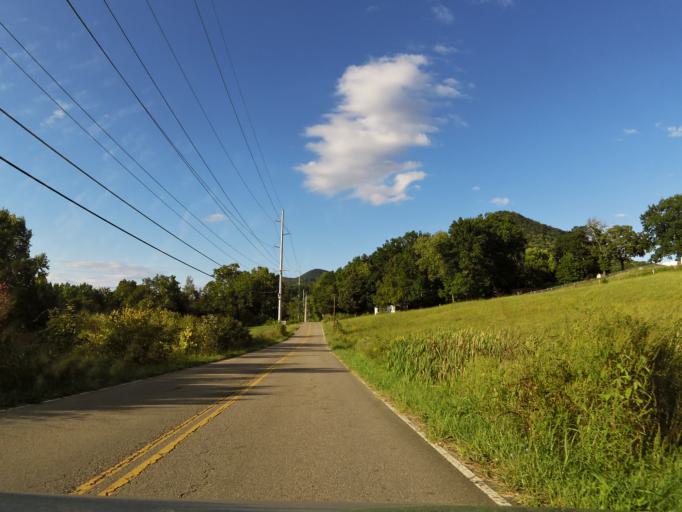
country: US
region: Tennessee
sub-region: Grainger County
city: Blaine
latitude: 36.1585
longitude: -83.7372
